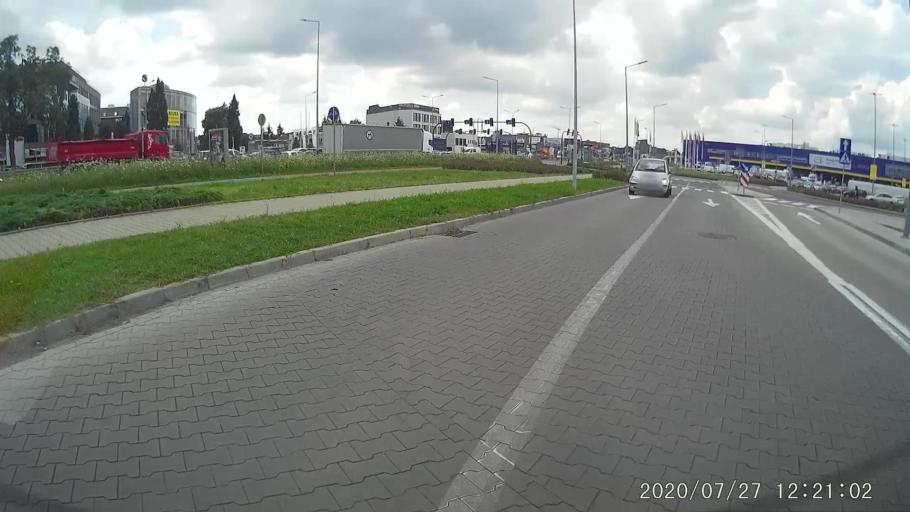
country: PL
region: Lesser Poland Voivodeship
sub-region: Powiat krakowski
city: Zielonki
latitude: 50.0891
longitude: 19.9005
